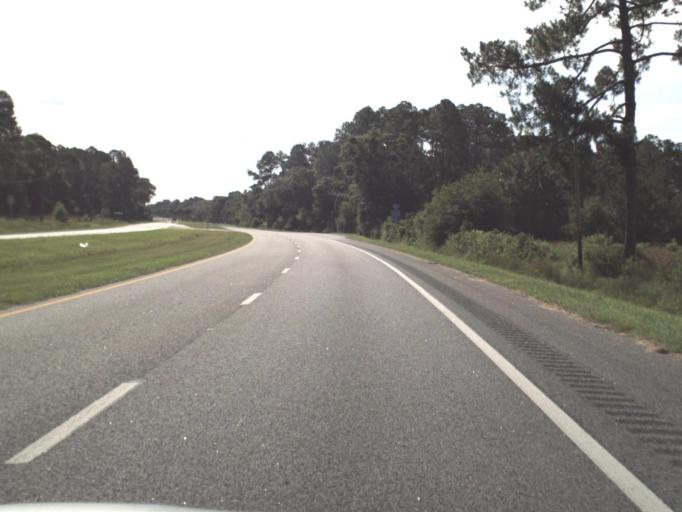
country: US
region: Florida
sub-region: Alachua County
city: Gainesville
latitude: 29.5145
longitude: -82.2919
